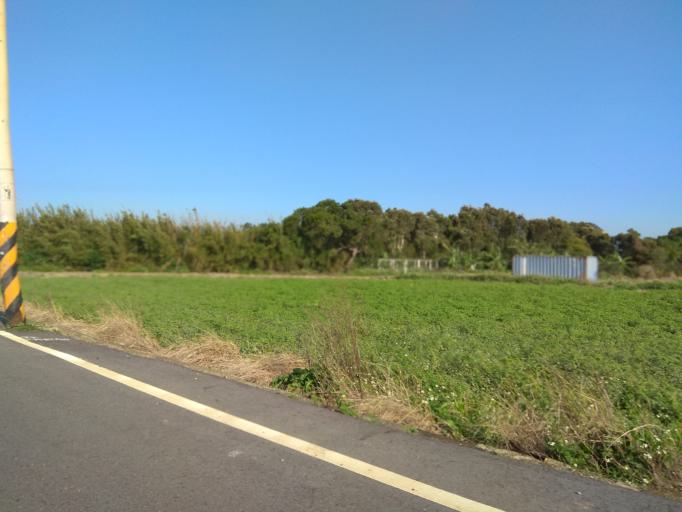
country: TW
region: Taiwan
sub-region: Hsinchu
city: Zhubei
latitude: 25.0030
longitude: 121.0518
